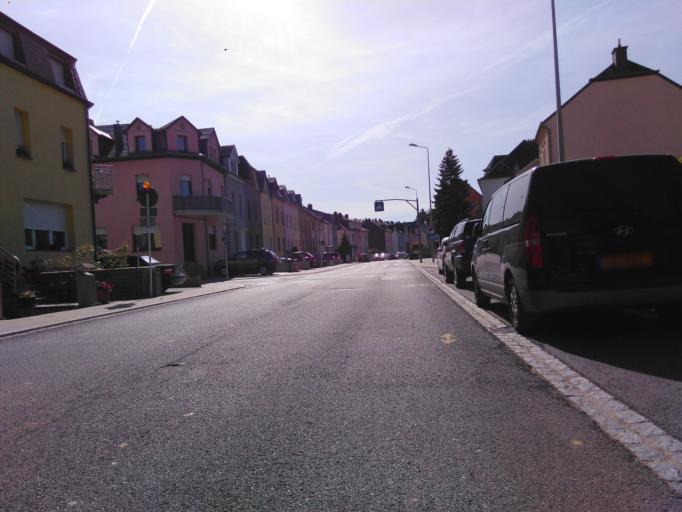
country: LU
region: Luxembourg
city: Tetange
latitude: 49.4805
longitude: 6.0371
